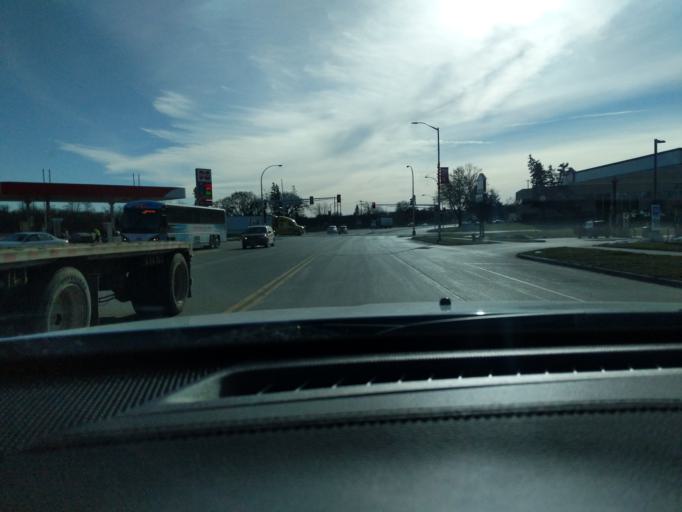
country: US
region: Minnesota
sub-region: Yellow Medicine County
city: Granite Falls
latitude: 44.8067
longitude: -95.5458
